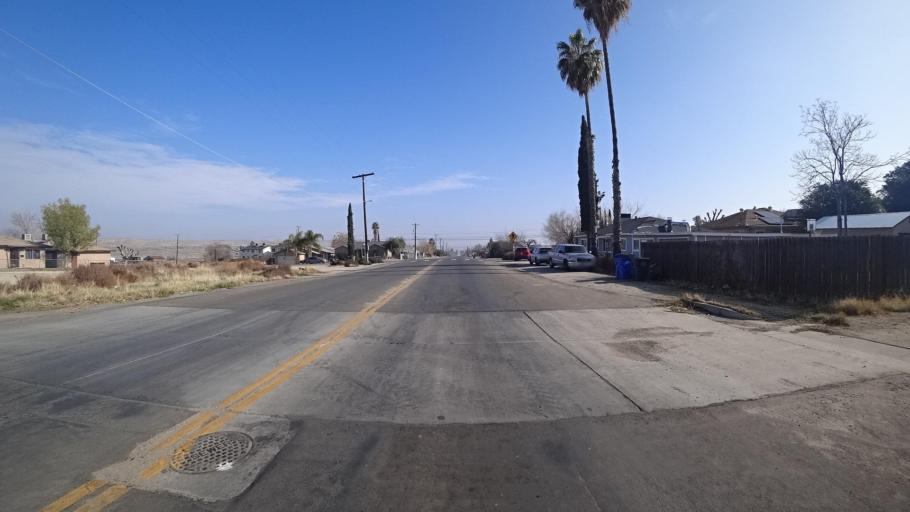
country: US
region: California
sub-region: Kern County
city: Ford City
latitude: 35.1545
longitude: -119.4532
